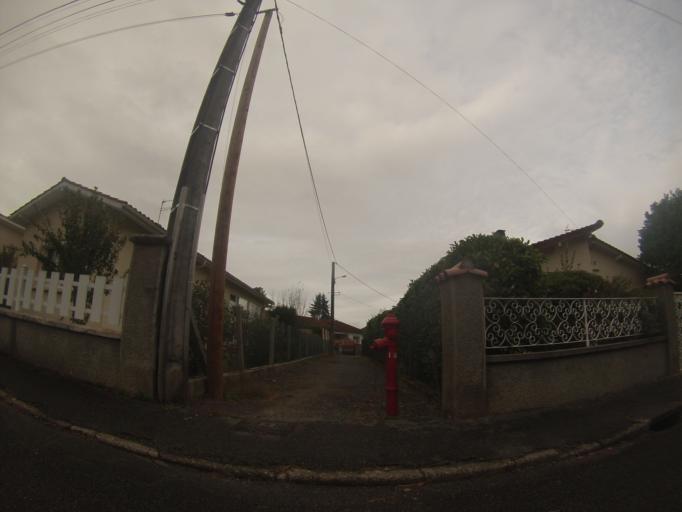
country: FR
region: Aquitaine
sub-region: Departement des Pyrenees-Atlantiques
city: Mazeres-Lezons
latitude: 43.2740
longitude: -0.3564
